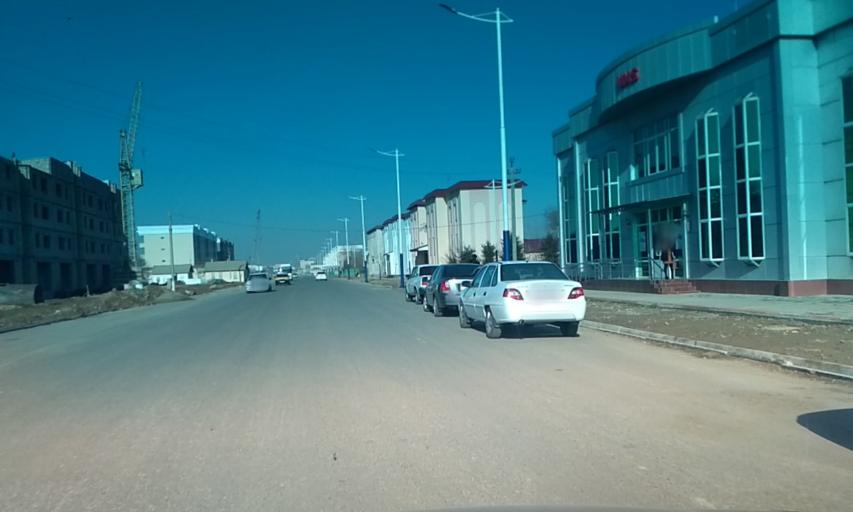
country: UZ
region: Sirdaryo
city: Guliston
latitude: 40.5007
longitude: 68.7722
